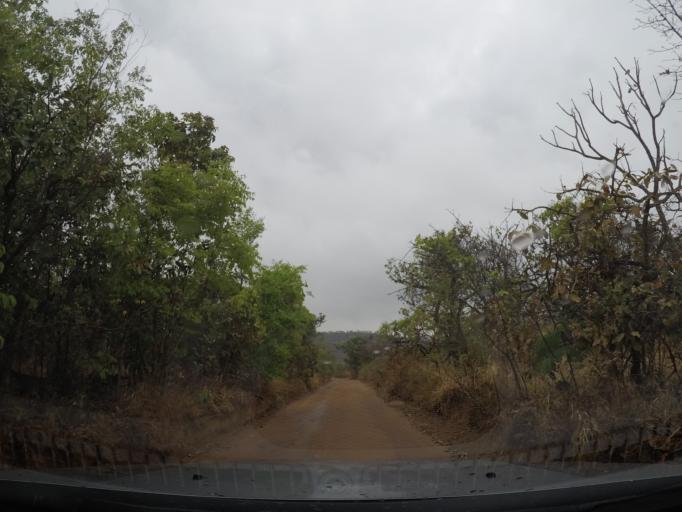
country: BR
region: Goias
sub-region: Pirenopolis
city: Pirenopolis
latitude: -15.8260
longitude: -48.8824
